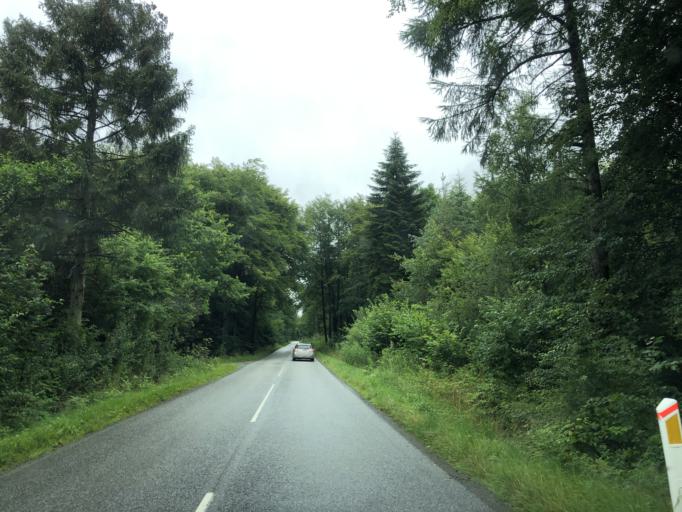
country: DK
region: South Denmark
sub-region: Vejle Kommune
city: Borkop
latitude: 55.6802
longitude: 9.6155
